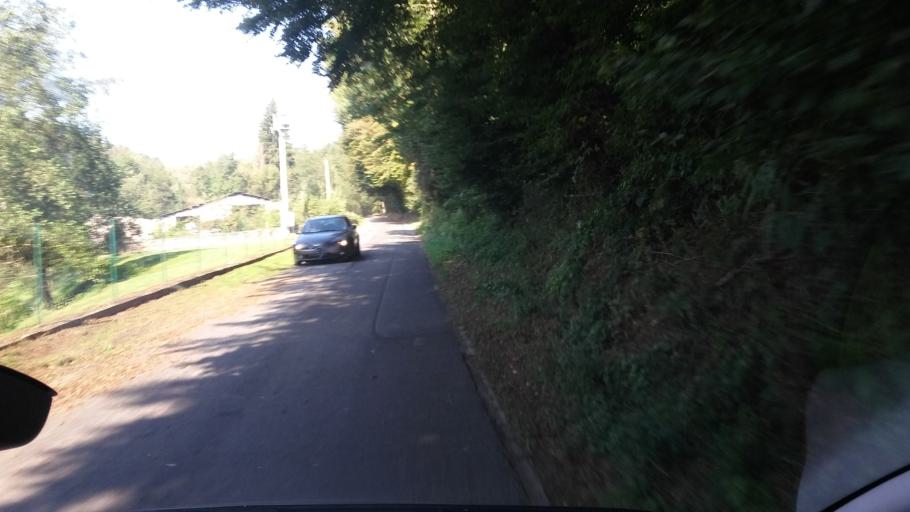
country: LU
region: Luxembourg
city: Eischen
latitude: 49.7009
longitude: 5.8568
